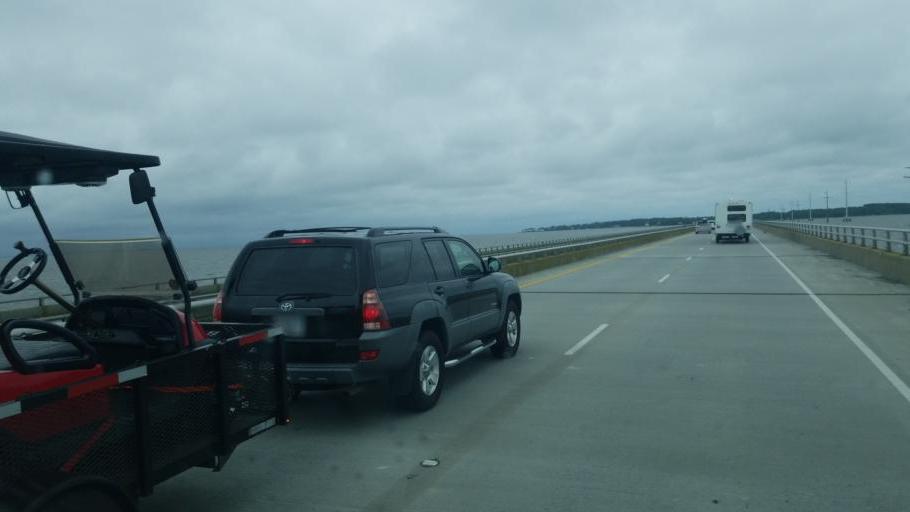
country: US
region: North Carolina
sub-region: Dare County
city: Southern Shores
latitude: 36.0865
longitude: -75.7693
